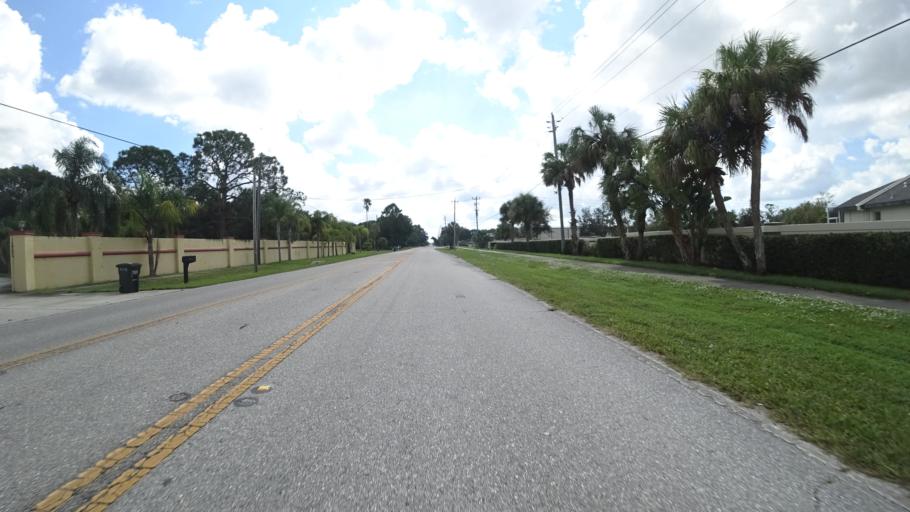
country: US
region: Florida
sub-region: Manatee County
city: Samoset
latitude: 27.4372
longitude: -82.5219
